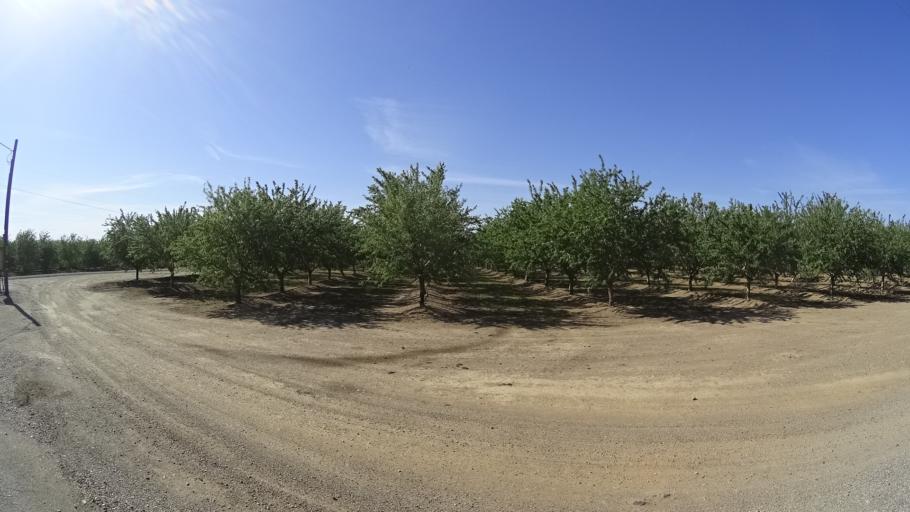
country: US
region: California
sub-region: Glenn County
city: Willows
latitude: 39.6113
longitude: -122.1840
